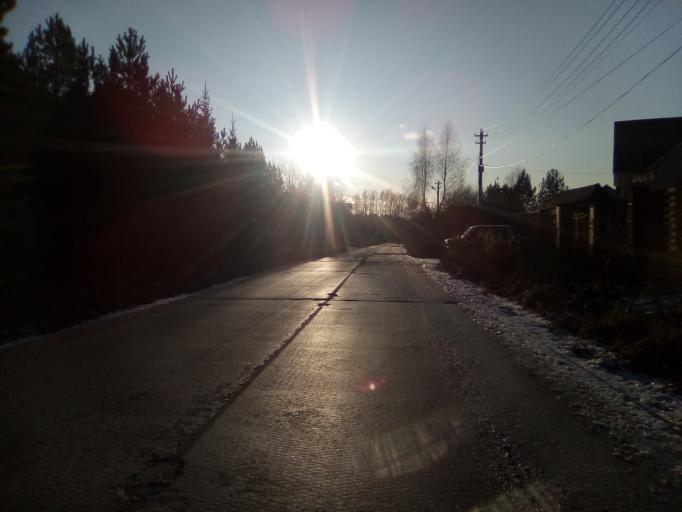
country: RU
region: Moskovskaya
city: Zhavoronki
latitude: 55.6446
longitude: 37.1483
